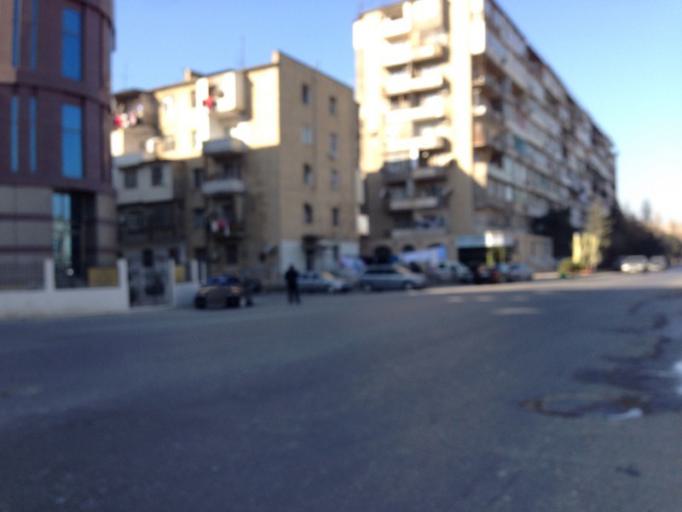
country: AZ
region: Baki
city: Baku
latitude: 40.4082
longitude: 49.8743
